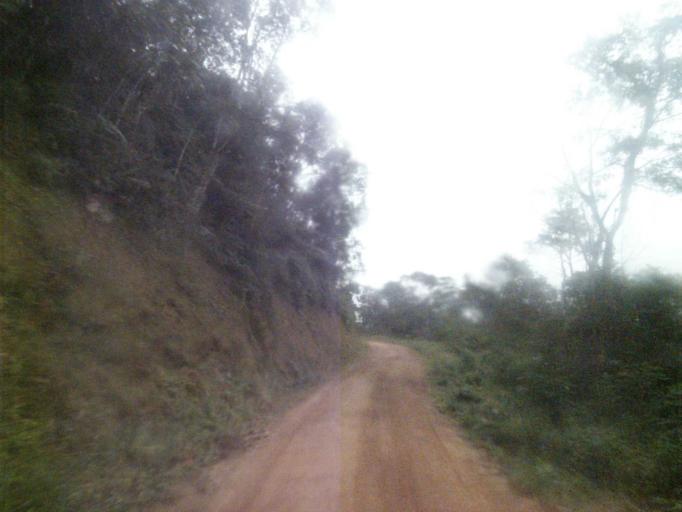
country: BR
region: Santa Catarina
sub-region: Anitapolis
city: Anitapolis
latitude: -27.8542
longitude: -49.1351
